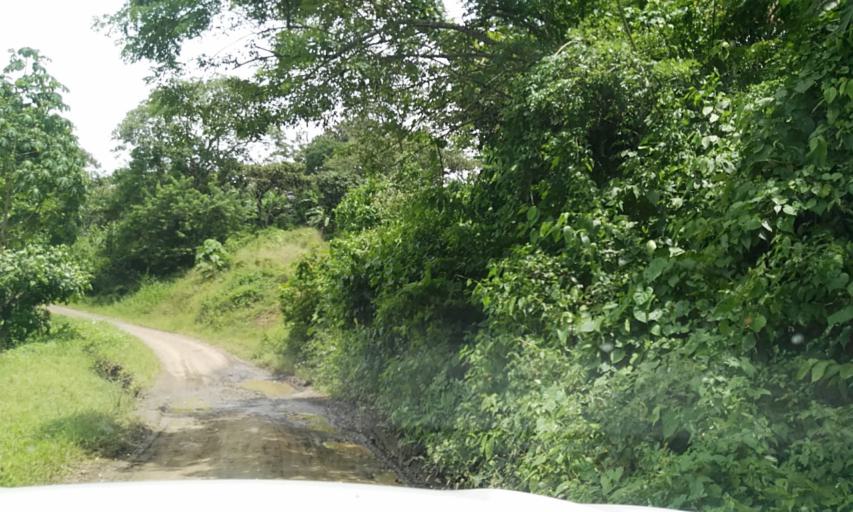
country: NI
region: Matagalpa
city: San Ramon
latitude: 12.9868
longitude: -85.8484
